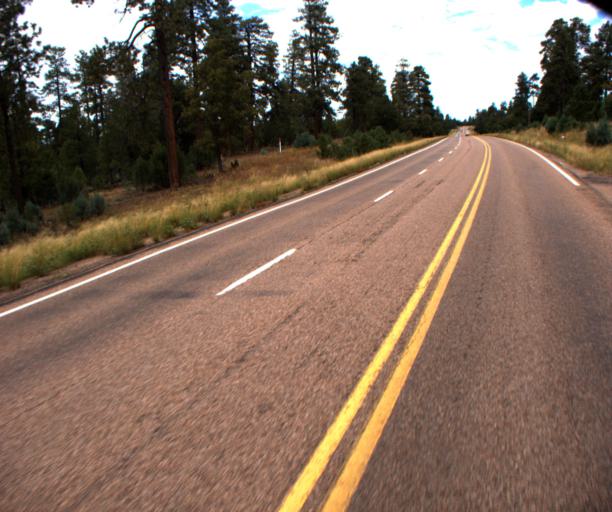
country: US
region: Arizona
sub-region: Navajo County
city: Heber-Overgaard
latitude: 34.3848
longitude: -110.6708
